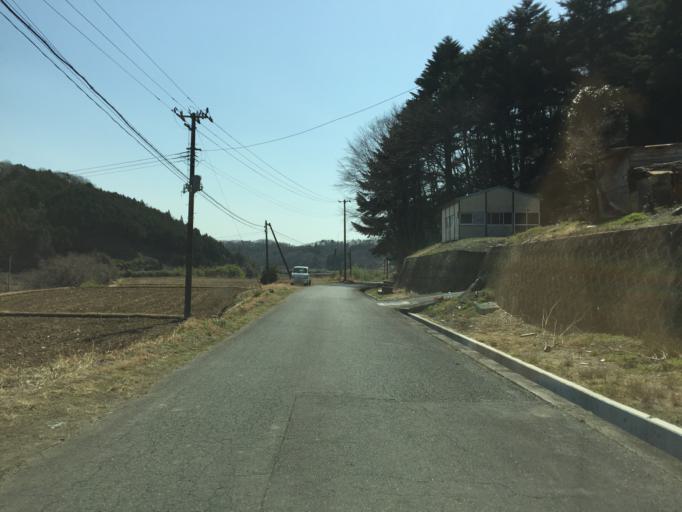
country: JP
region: Fukushima
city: Iwaki
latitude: 37.0069
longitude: 140.7940
